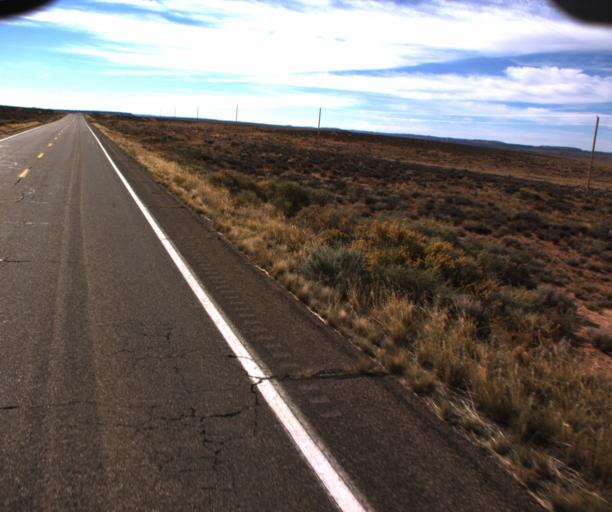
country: US
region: Arizona
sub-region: Coconino County
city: LeChee
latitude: 36.7290
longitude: -111.2818
